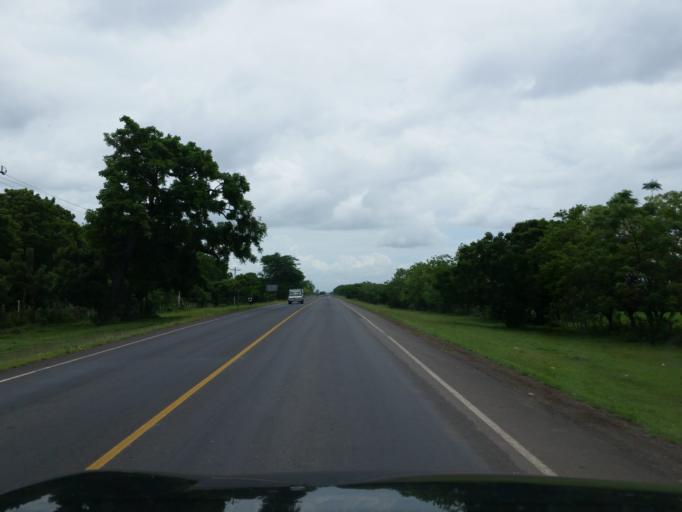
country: NI
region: Managua
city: Tipitapa
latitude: 12.3510
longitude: -86.0494
